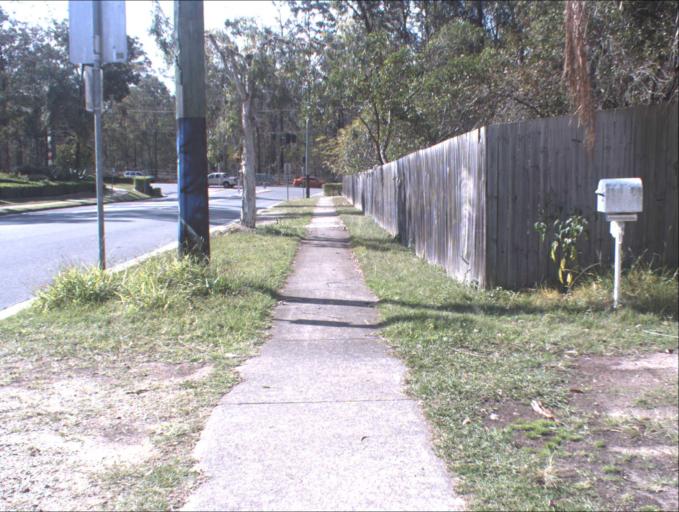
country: AU
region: Queensland
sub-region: Brisbane
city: Forest Lake
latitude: -27.6572
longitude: 153.0075
